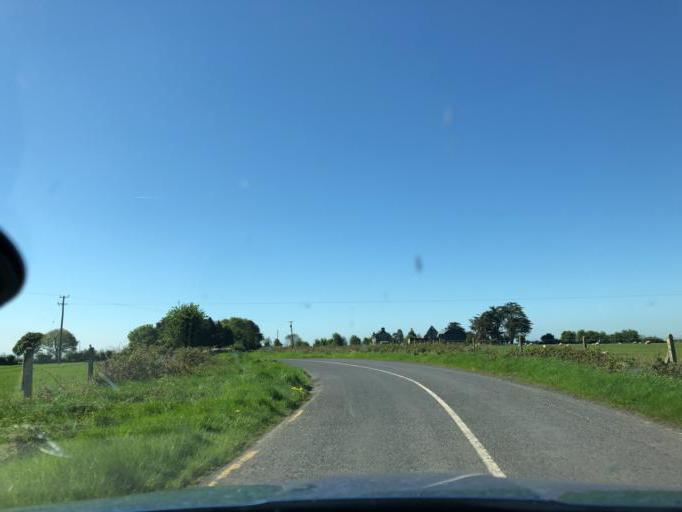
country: IE
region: Connaught
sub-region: County Galway
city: Portumna
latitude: 53.1712
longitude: -8.2098
